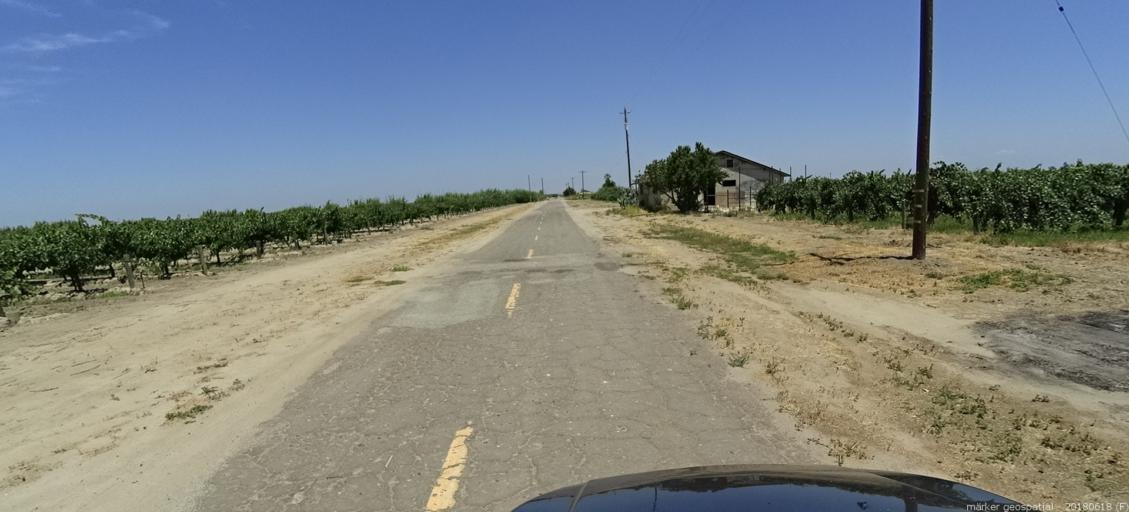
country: US
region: California
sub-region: Madera County
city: Parkwood
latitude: 36.8982
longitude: -120.1196
